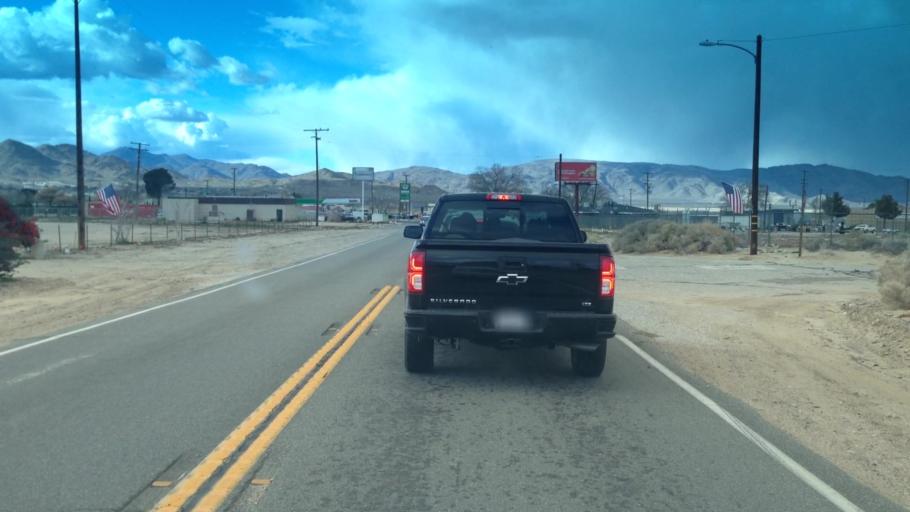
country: US
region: California
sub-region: San Bernardino County
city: Lucerne Valley
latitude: 34.4421
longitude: -116.9481
